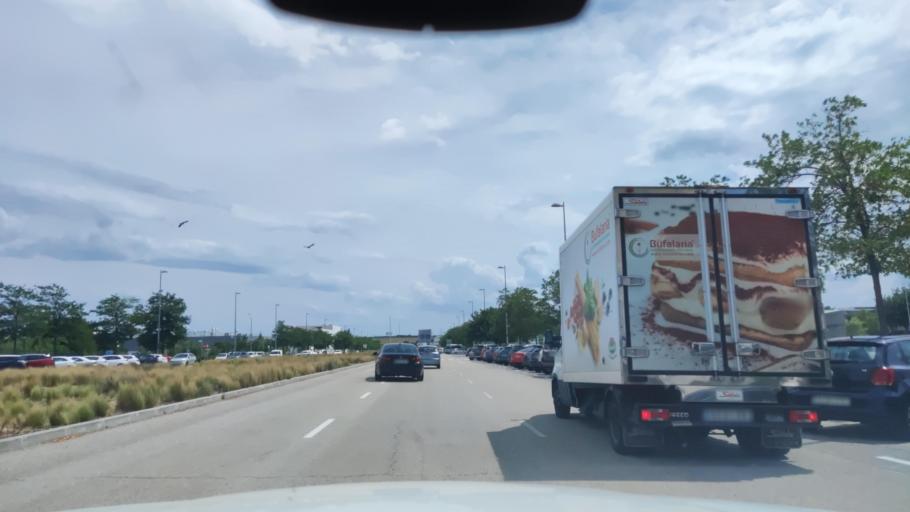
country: ES
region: Madrid
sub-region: Provincia de Madrid
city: Barajas de Madrid
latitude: 40.4872
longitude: -3.6086
